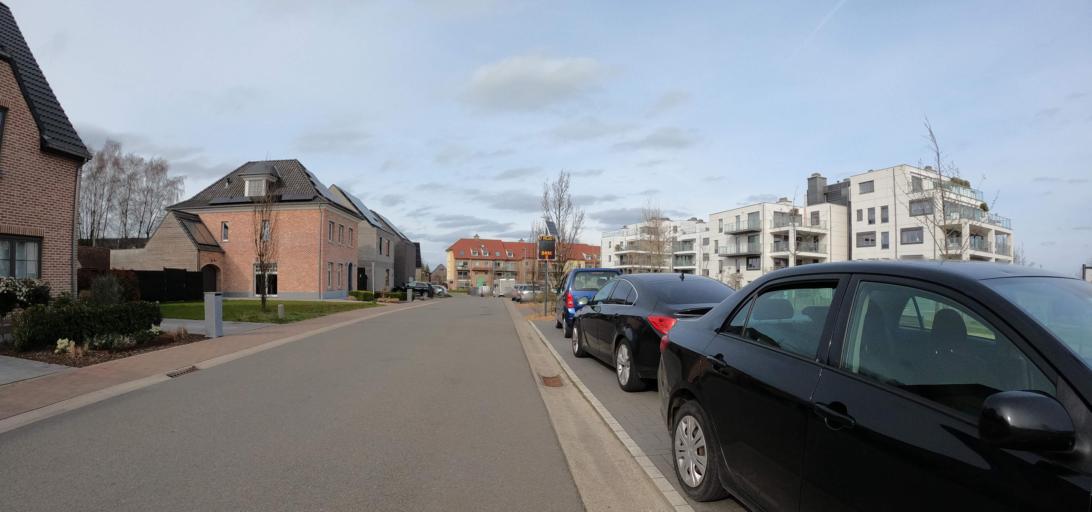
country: BE
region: Flanders
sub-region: Provincie Oost-Vlaanderen
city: Sint-Niklaas
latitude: 51.1772
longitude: 4.1565
